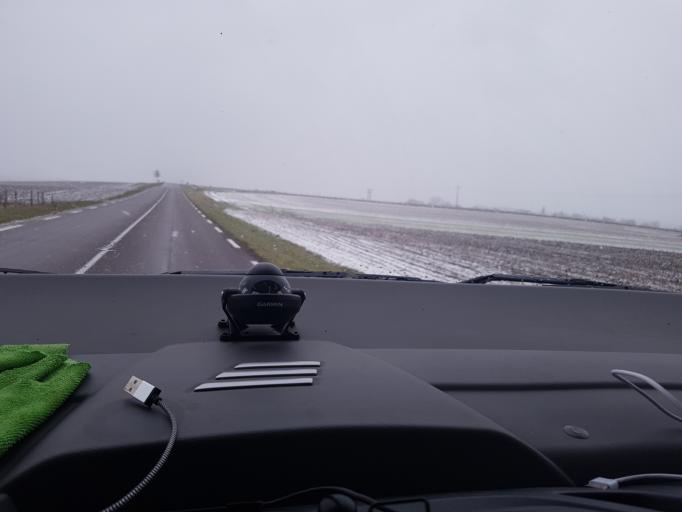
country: FR
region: Lorraine
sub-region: Departement de la Moselle
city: Dieuze
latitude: 48.7460
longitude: 6.6470
